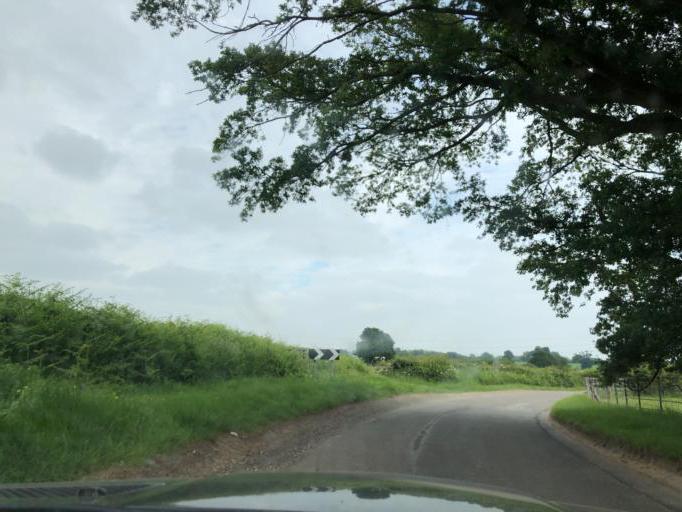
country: GB
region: England
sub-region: Warwickshire
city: Kenilworth
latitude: 52.3354
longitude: -1.6202
